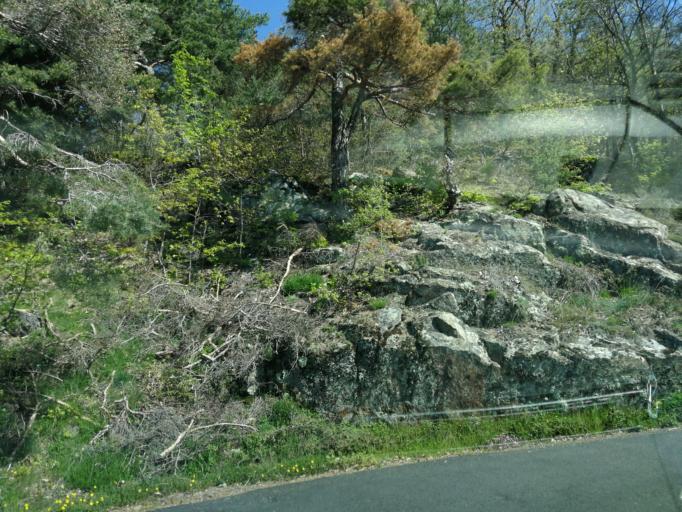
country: FR
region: Rhone-Alpes
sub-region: Departement de l'Ardeche
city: Le Cheylard
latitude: 44.9235
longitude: 4.4185
